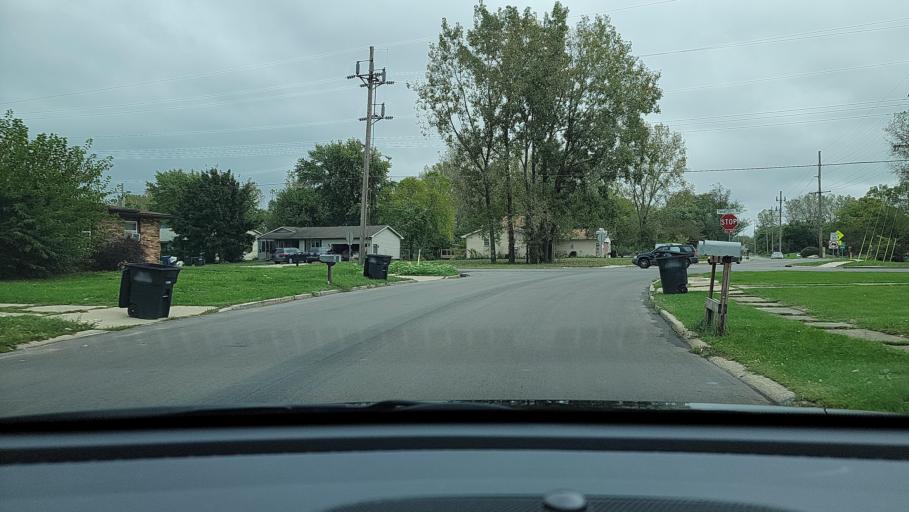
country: US
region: Indiana
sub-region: Porter County
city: Portage
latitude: 41.5579
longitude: -87.1979
